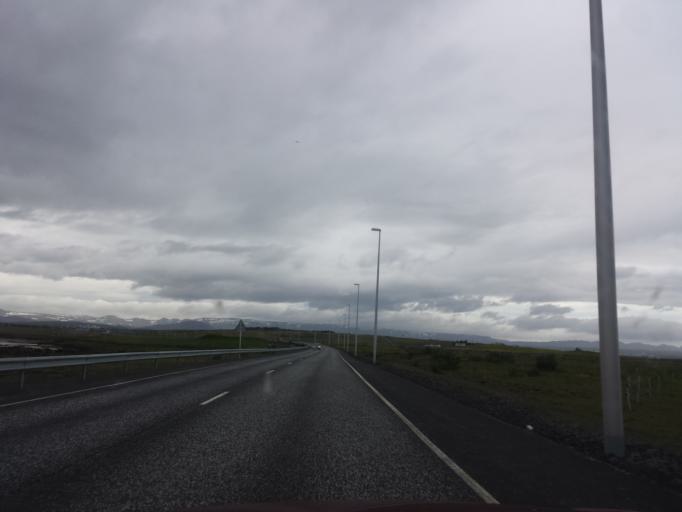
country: IS
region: Capital Region
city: Alftanes
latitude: 64.1004
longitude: -22.0080
